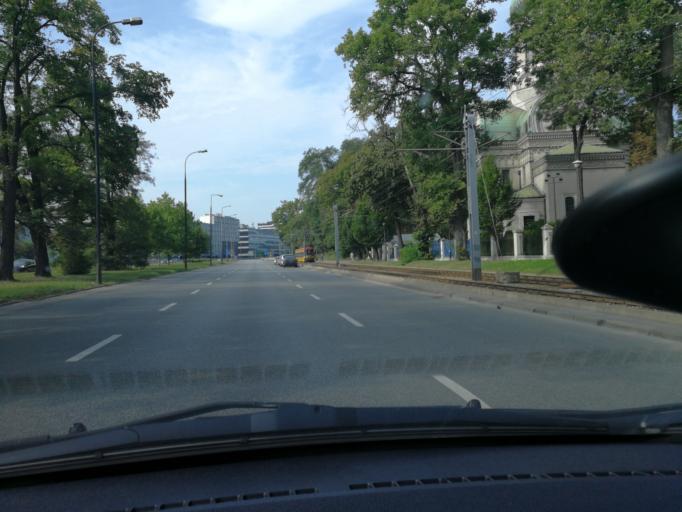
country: PL
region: Masovian Voivodeship
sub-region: Warszawa
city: Ochota
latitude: 52.2280
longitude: 20.9474
